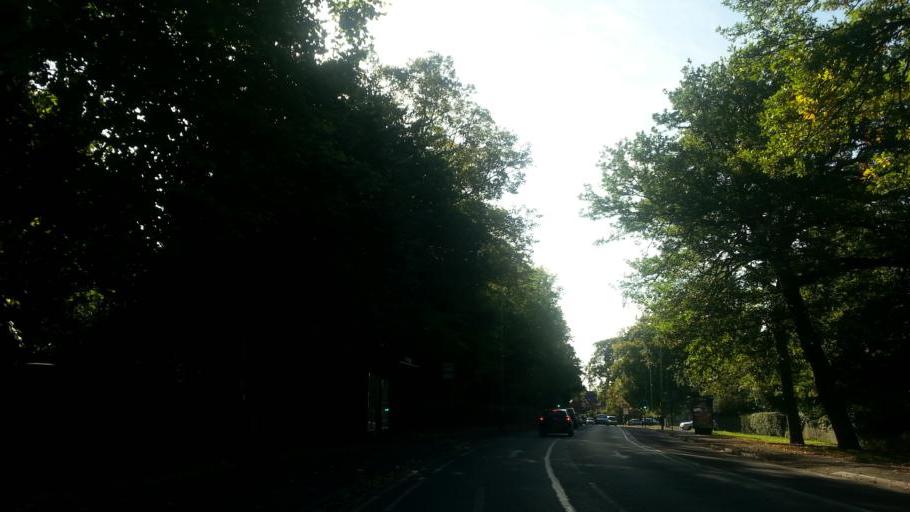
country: GB
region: England
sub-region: Leicestershire
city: Oadby
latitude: 52.6113
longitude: -1.1009
